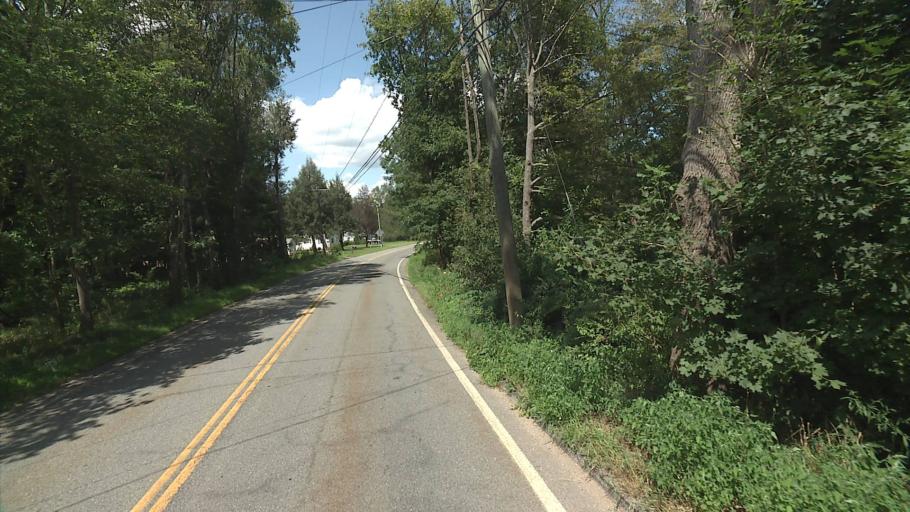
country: US
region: Connecticut
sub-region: Tolland County
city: Mansfield City
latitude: 41.7669
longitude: -72.1961
